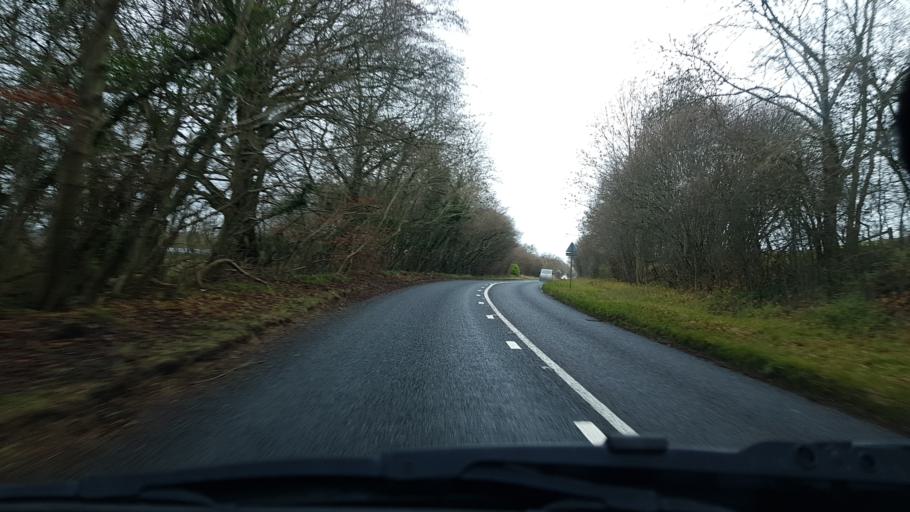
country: GB
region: England
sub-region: Gloucestershire
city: Charlton Kings
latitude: 51.8251
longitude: -2.0389
